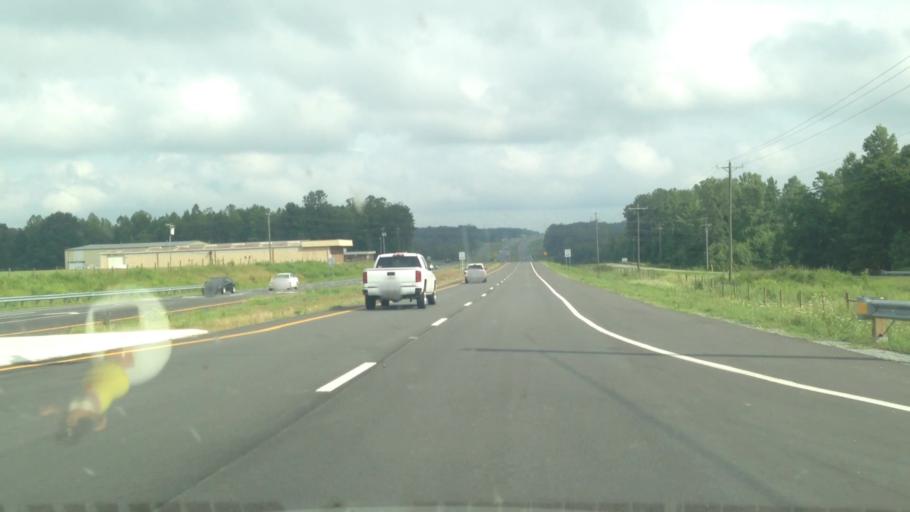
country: US
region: North Carolina
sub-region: Guilford County
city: Summerfield
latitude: 36.2202
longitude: -79.9100
